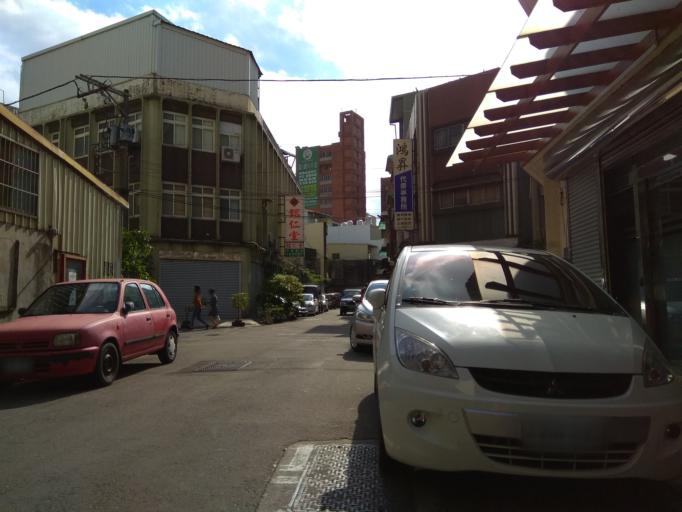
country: TW
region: Taiwan
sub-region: Hsinchu
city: Hsinchu
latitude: 24.7977
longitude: 120.9760
